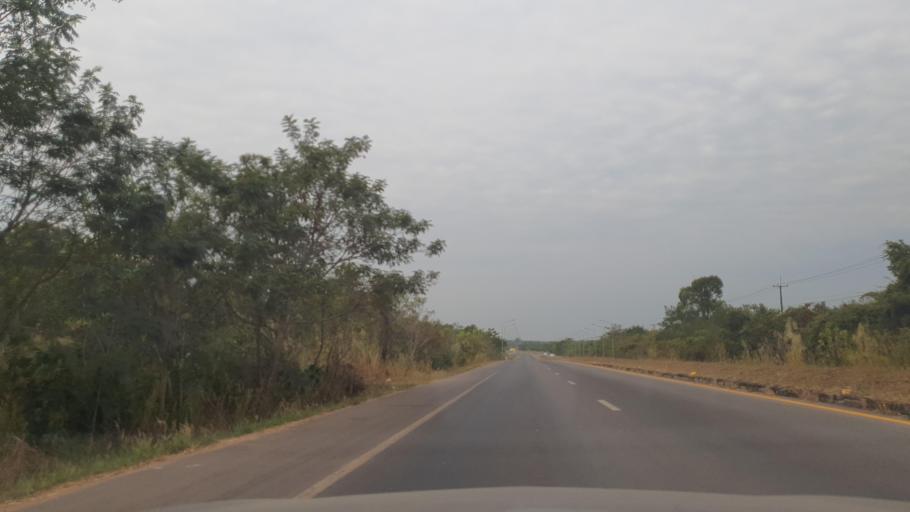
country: TH
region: Changwat Bueng Kan
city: Bung Khla
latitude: 18.2984
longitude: 103.9789
